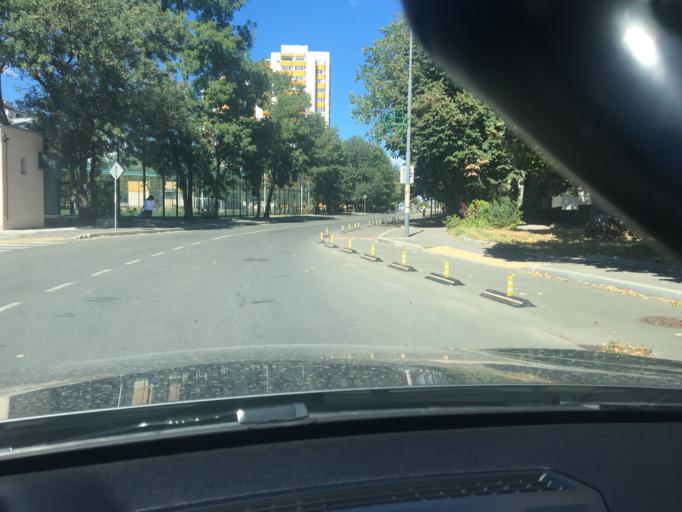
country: BG
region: Burgas
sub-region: Obshtina Burgas
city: Burgas
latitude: 42.5280
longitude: 27.4637
